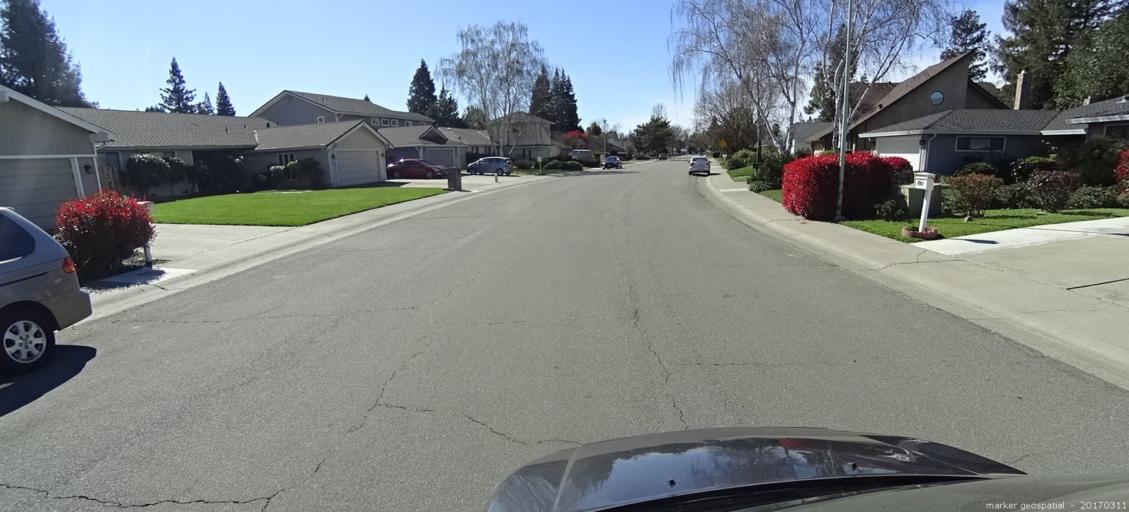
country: US
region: California
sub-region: Sacramento County
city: Parkway
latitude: 38.4941
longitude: -121.5426
